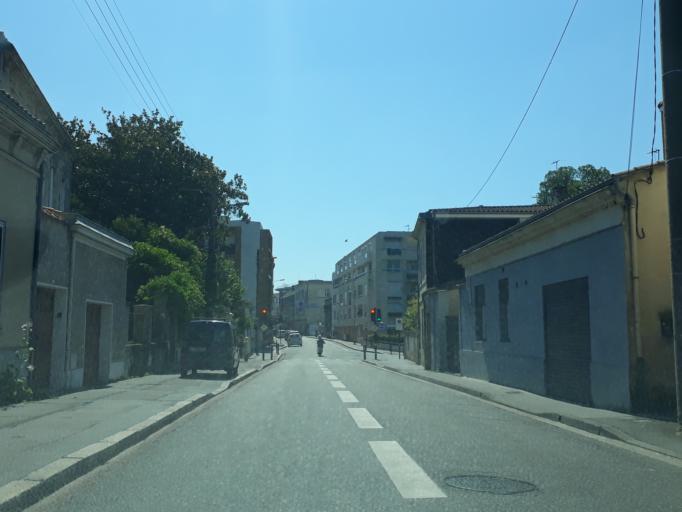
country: FR
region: Aquitaine
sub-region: Departement de la Gironde
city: Merignac
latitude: 44.8373
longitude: -0.6076
